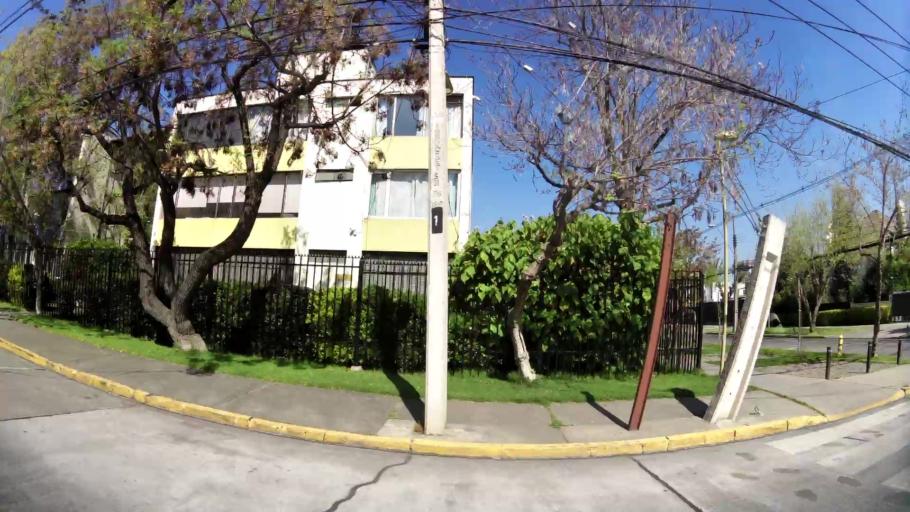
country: CL
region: Santiago Metropolitan
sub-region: Provincia de Santiago
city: Villa Presidente Frei, Nunoa, Santiago, Chile
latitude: -33.4205
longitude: -70.5848
